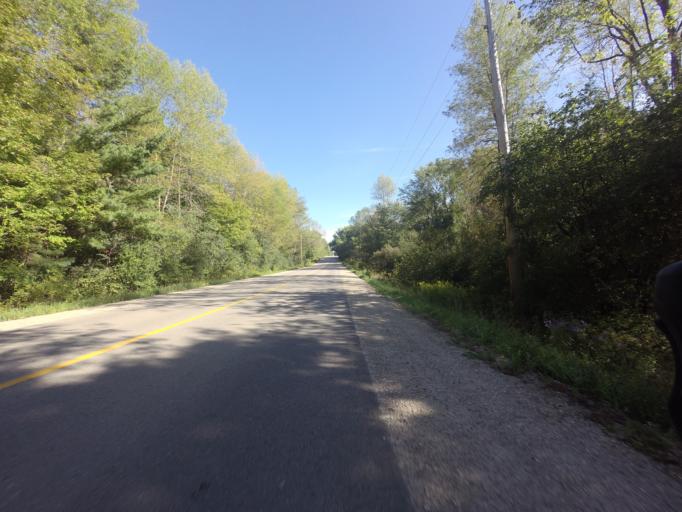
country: CA
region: Ontario
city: Perth
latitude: 44.9060
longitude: -76.3375
